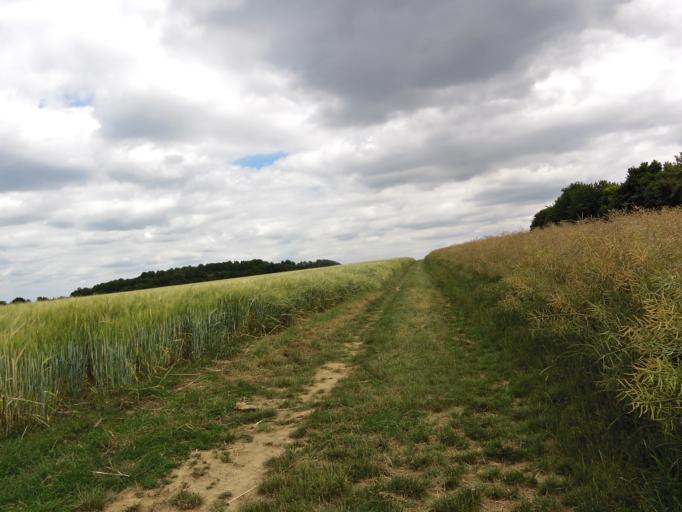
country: DE
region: Bavaria
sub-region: Regierungsbezirk Unterfranken
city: Randersacker
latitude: 49.7694
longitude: 9.9710
